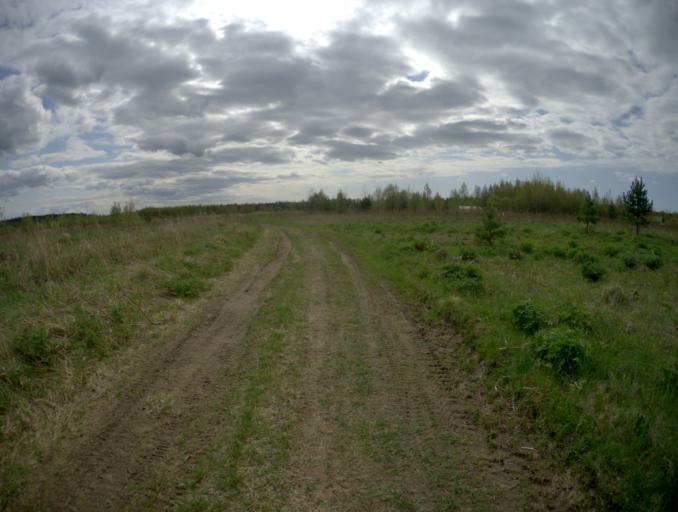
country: RU
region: Vladimir
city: Golovino
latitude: 55.9455
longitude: 40.4109
